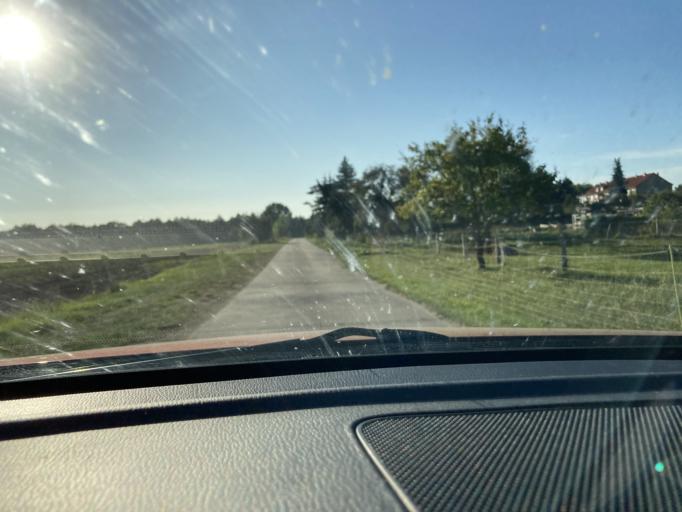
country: DE
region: Mecklenburg-Vorpommern
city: Alt-Sanitz
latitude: 53.7490
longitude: 13.6284
